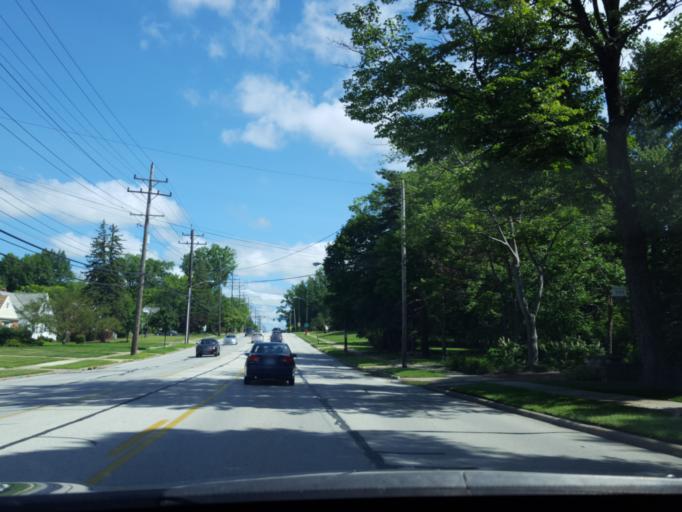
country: US
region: Ohio
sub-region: Cuyahoga County
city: Lyndhurst
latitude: 41.5330
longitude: -81.4971
